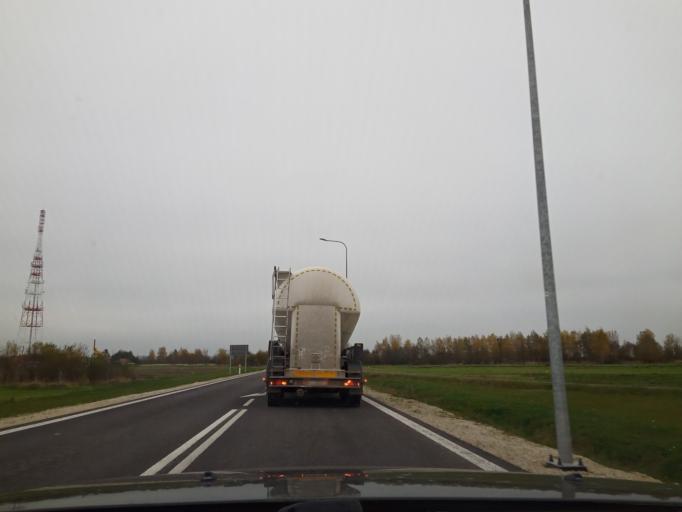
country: PL
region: Swietokrzyskie
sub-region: Powiat jedrzejowski
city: Jedrzejow
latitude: 50.6193
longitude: 20.3133
